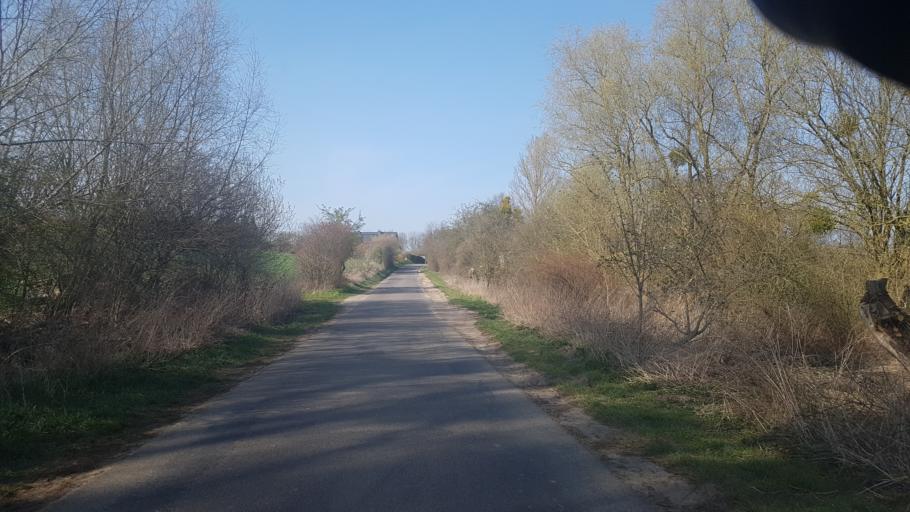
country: DE
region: Brandenburg
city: Gerswalde
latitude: 53.2023
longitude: 13.7824
